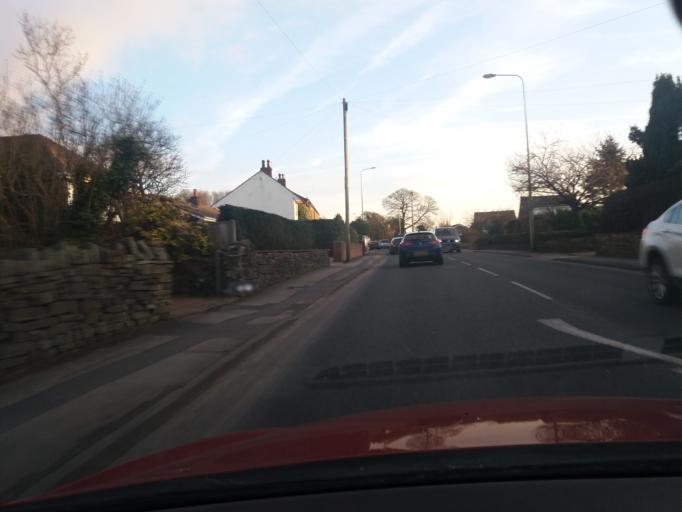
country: GB
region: England
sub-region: Lancashire
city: Chorley
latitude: 53.6776
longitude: -2.6162
